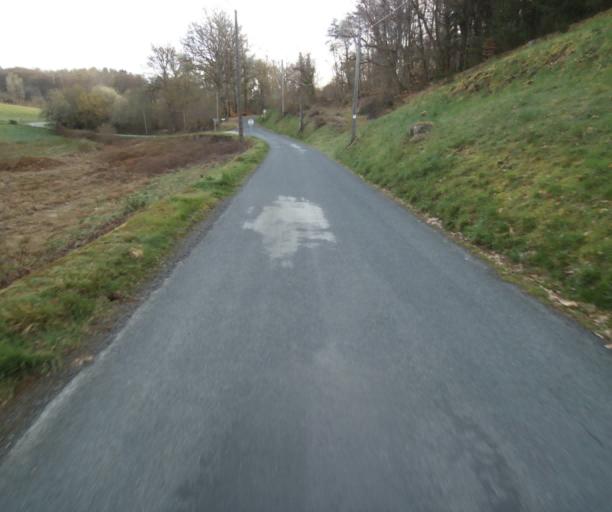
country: FR
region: Limousin
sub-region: Departement de la Correze
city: Correze
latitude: 45.3760
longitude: 1.8783
